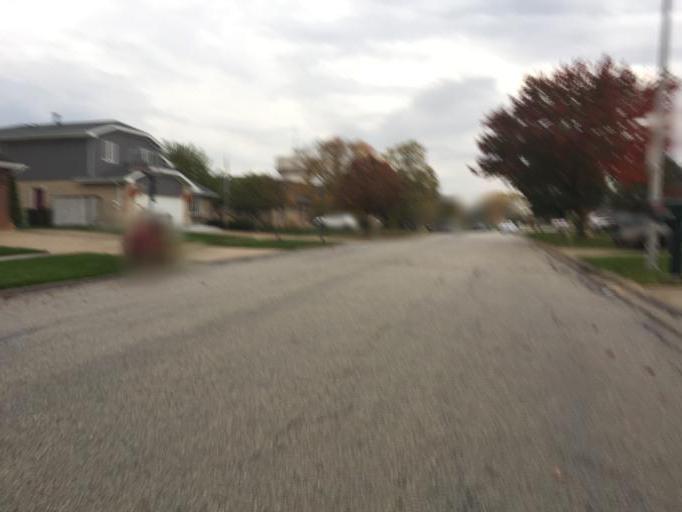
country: US
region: Illinois
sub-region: Cook County
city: Tinley Park
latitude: 41.5679
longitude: -87.8148
